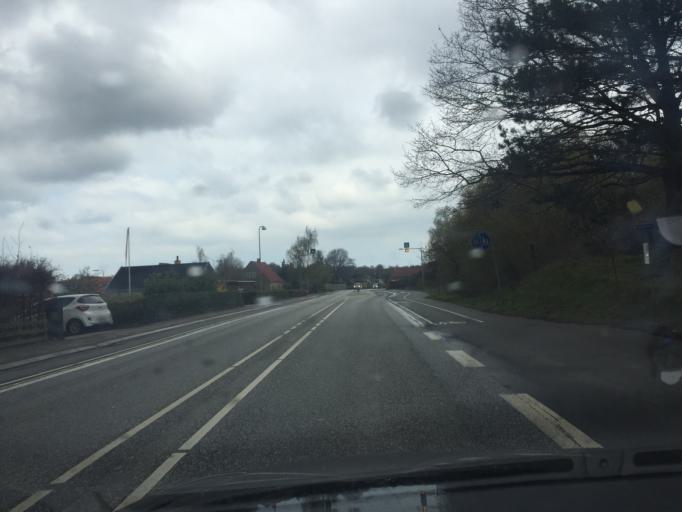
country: DK
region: Capital Region
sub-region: Halsnaes Kommune
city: Frederiksvaerk
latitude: 55.9919
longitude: 12.0144
